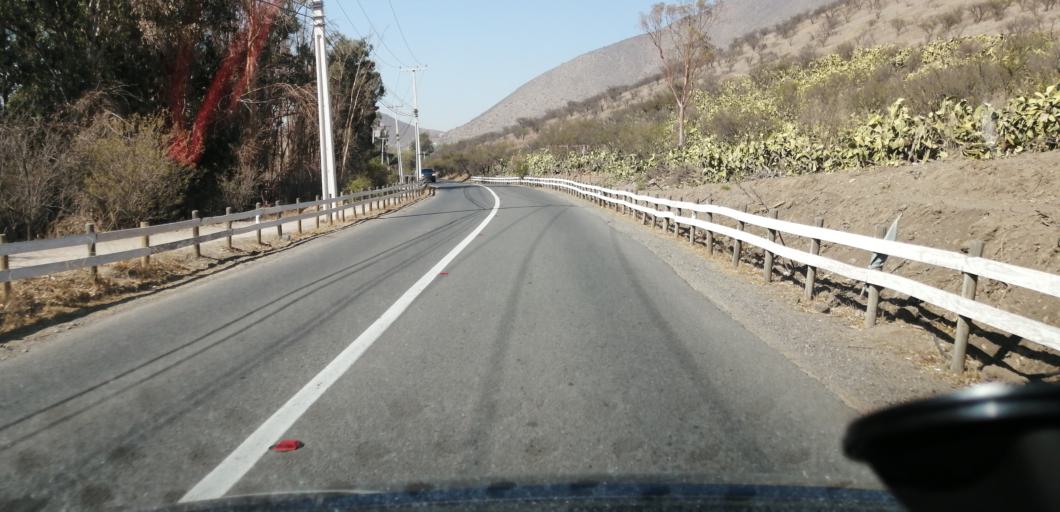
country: CL
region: Santiago Metropolitan
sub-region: Provincia de Santiago
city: Lo Prado
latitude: -33.4425
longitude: -70.8259
